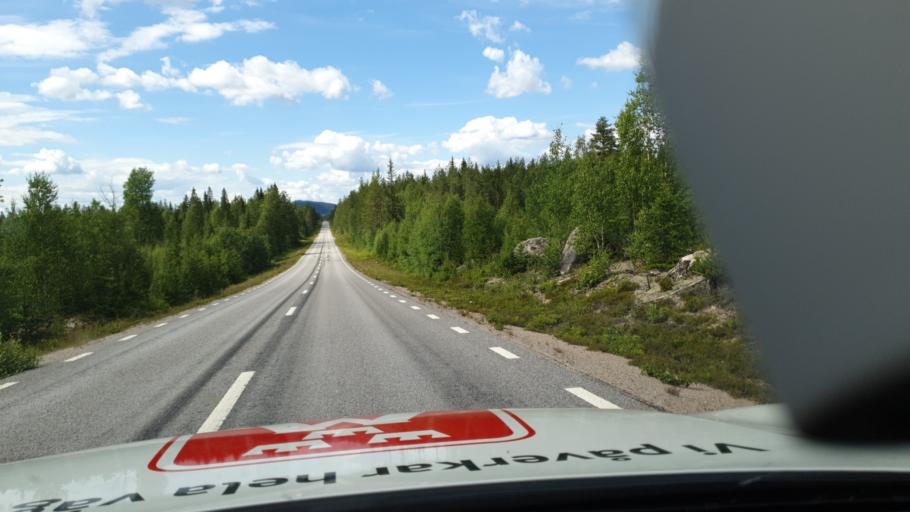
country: SE
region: Jaemtland
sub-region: Harjedalens Kommun
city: Sveg
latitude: 61.9826
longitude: 15.0676
